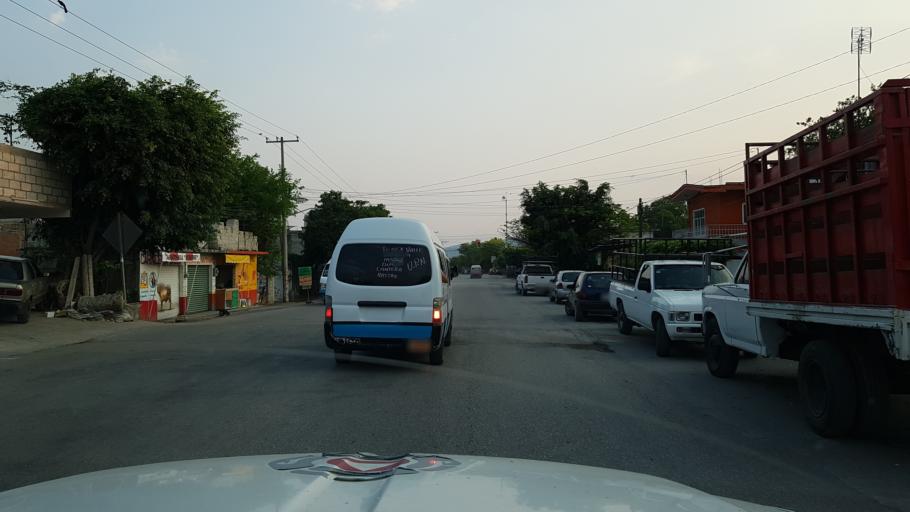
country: MX
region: Morelos
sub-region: Ayala
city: Olintepec
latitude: 18.7394
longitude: -98.9864
